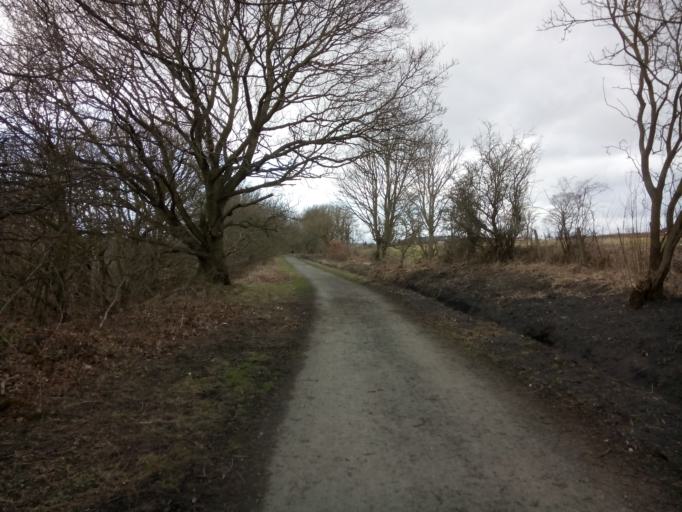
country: GB
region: England
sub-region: County Durham
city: Ushaw Moor
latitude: 54.7702
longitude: -1.6296
